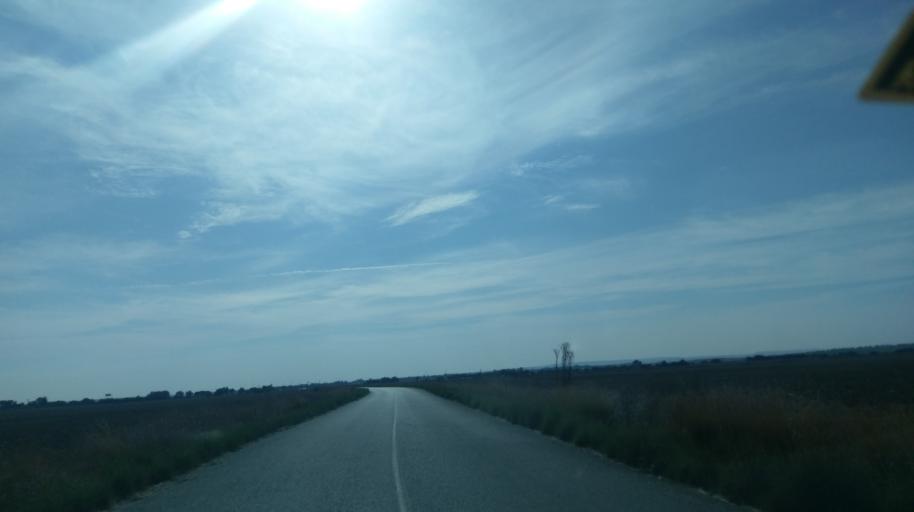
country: CY
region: Ammochostos
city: Lefkonoiko
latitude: 35.1904
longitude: 33.6993
